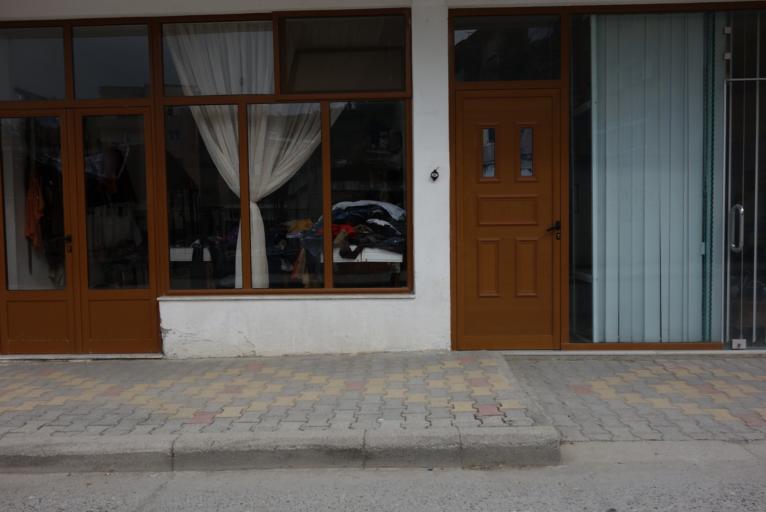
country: AL
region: Gjirokaster
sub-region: Rrethi i Permetit
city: Permet
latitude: 40.2326
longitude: 20.3522
